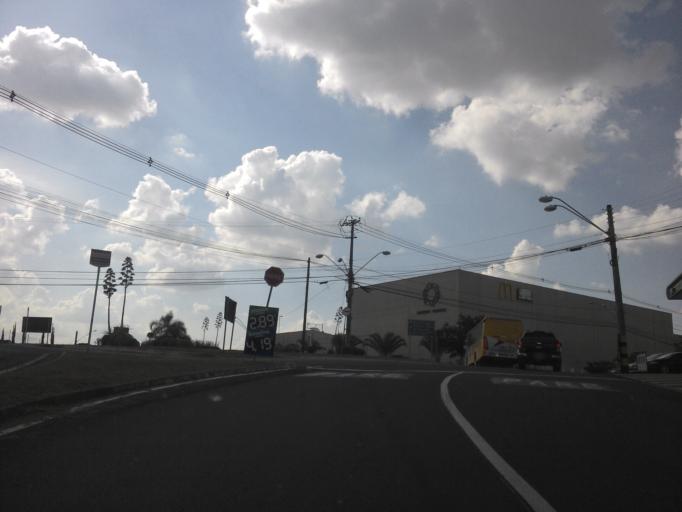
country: BR
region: Sao Paulo
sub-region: Valinhos
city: Valinhos
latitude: -22.9827
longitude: -47.0134
